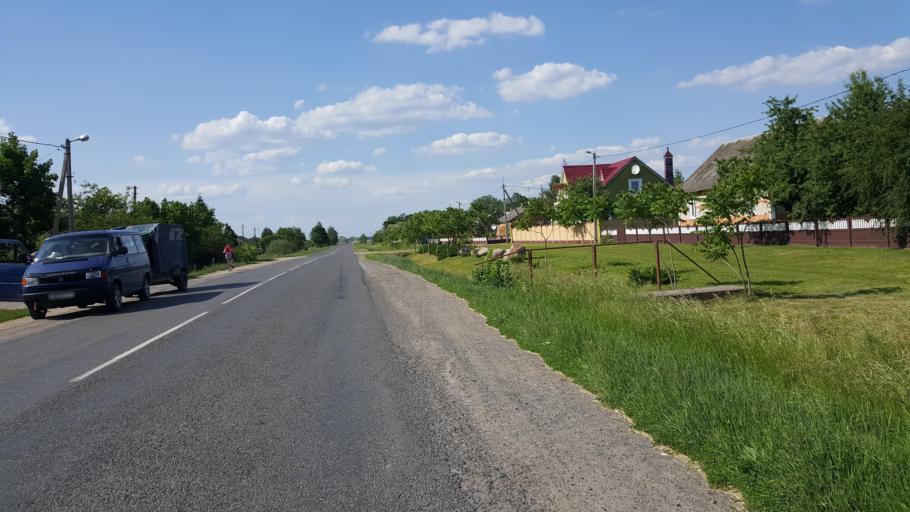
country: BY
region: Brest
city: Kobryn
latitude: 52.3039
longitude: 24.2742
